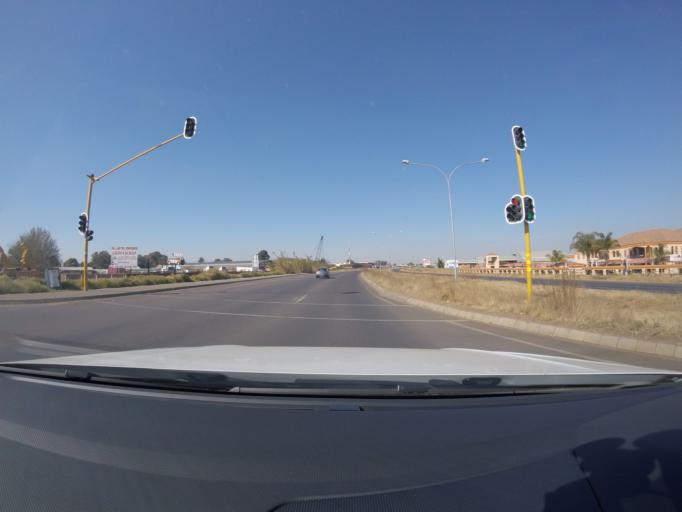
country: ZA
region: Gauteng
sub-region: Ekurhuleni Metropolitan Municipality
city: Benoni
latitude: -26.1196
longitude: 28.2805
